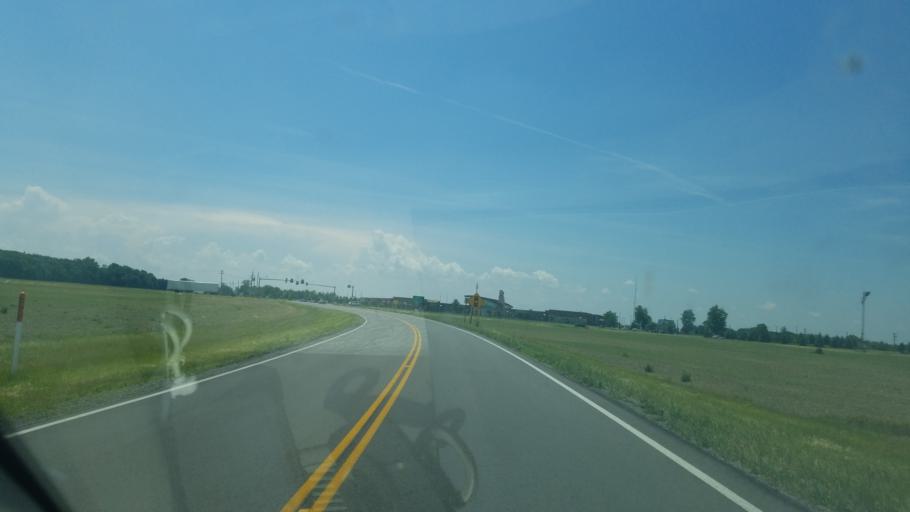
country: US
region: Ohio
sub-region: Hancock County
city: Findlay
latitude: 41.0828
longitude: -83.6180
